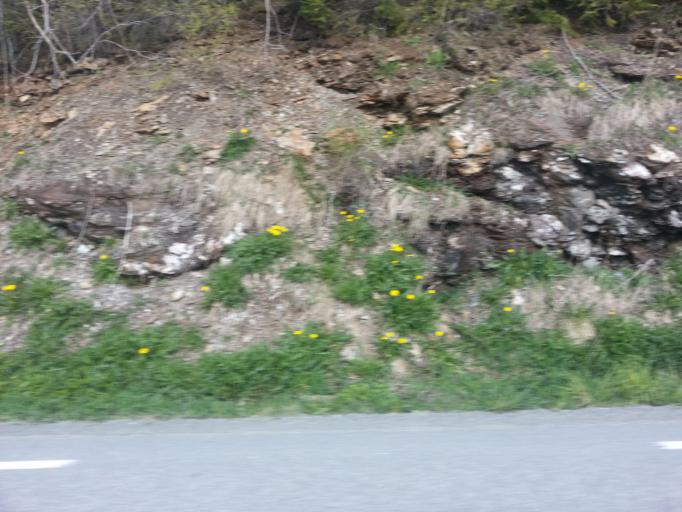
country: NO
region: Nord-Trondelag
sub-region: Levanger
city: Skogn
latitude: 63.6422
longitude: 11.2548
